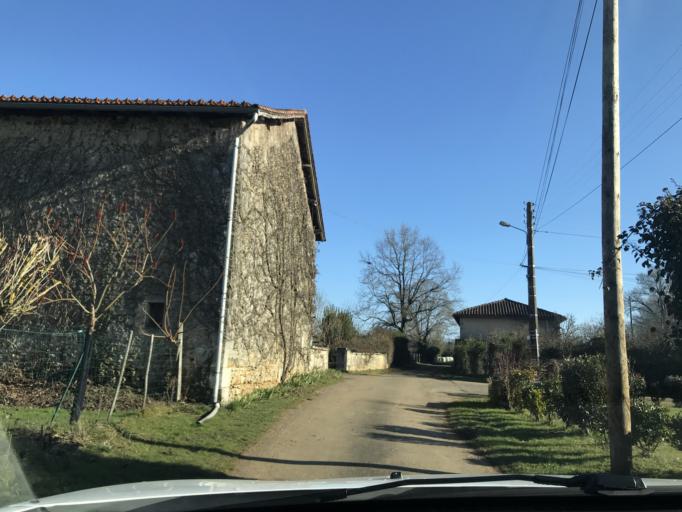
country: FR
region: Poitou-Charentes
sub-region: Departement de la Charente
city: Saint-Claud
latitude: 45.8450
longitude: 0.5181
